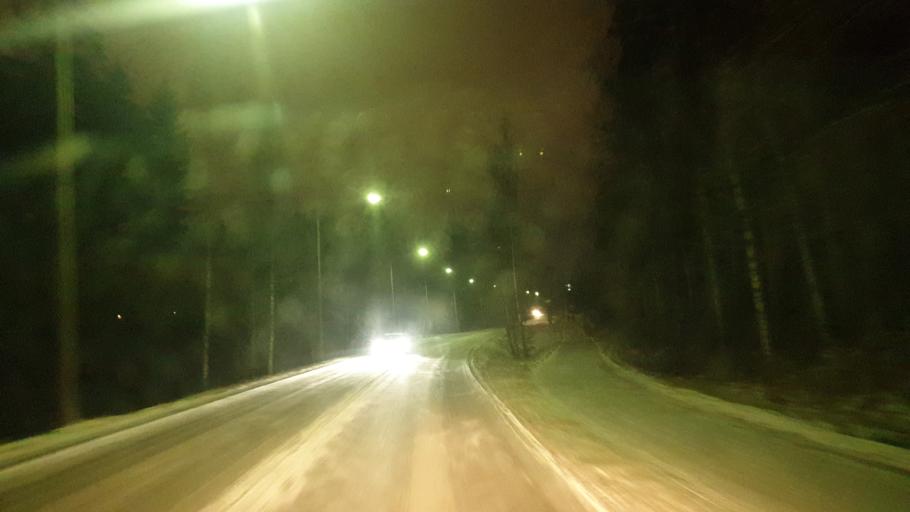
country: FI
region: Southern Savonia
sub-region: Savonlinna
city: Savonlinna
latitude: 61.8611
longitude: 28.9462
